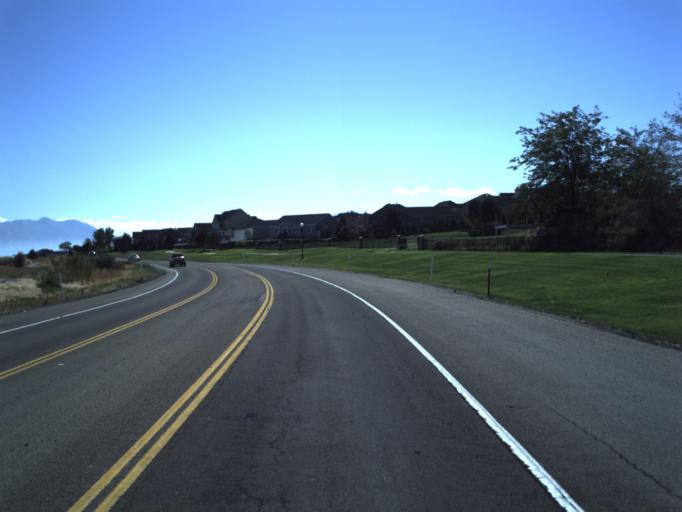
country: US
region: Utah
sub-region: Utah County
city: Saratoga Springs
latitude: 40.3194
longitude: -111.9001
